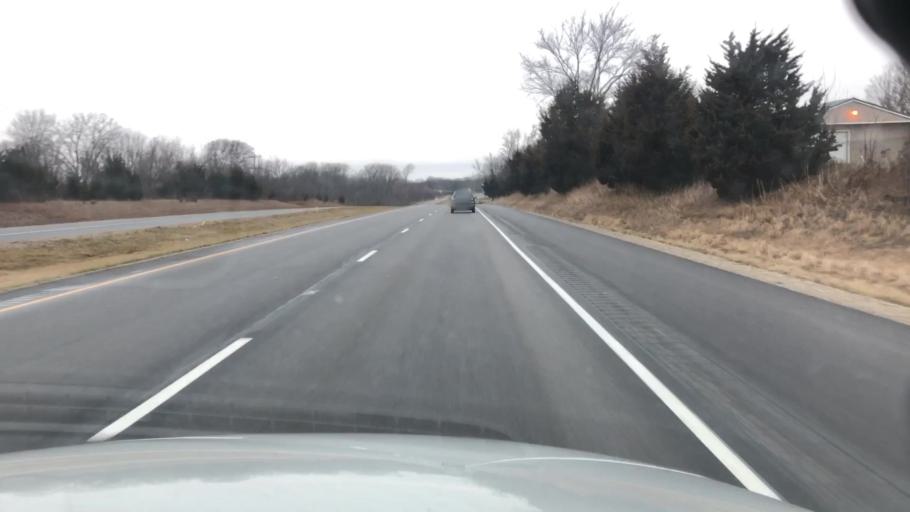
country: US
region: Indiana
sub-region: Kosciusko County
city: Pierceton
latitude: 41.1965
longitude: -85.6858
